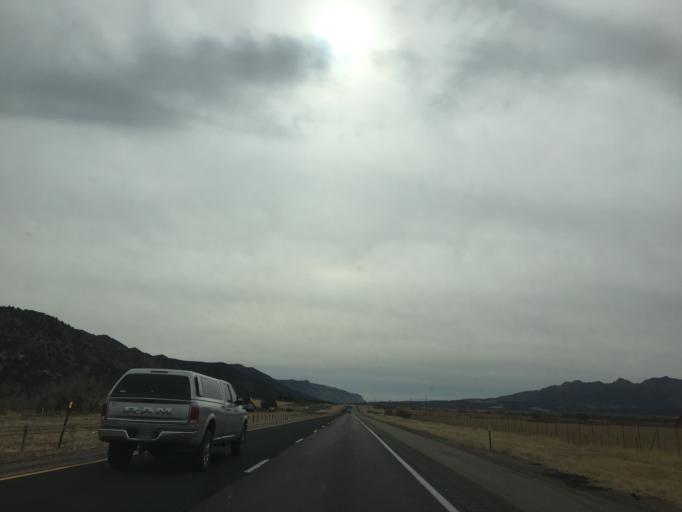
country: US
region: Utah
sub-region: Iron County
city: Cedar City
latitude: 37.4935
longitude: -113.2178
